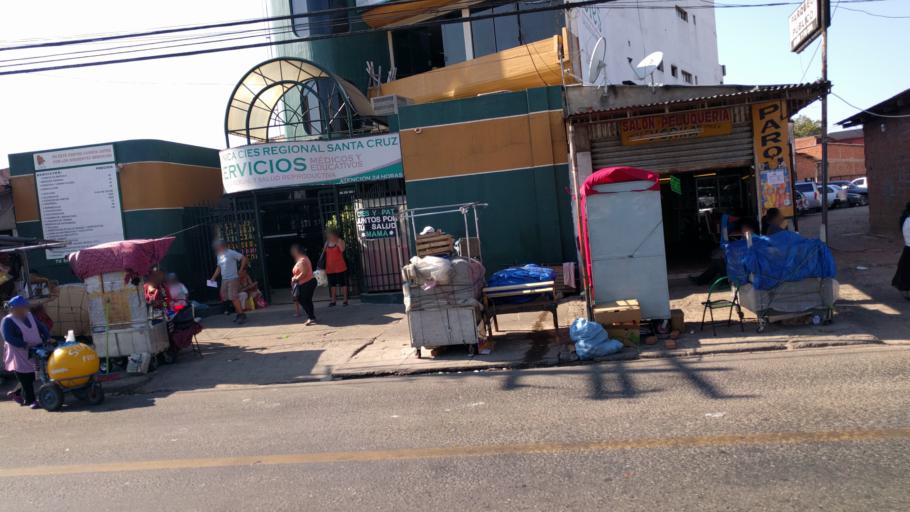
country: BO
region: Santa Cruz
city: Santa Cruz de la Sierra
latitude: -17.7959
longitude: -63.1902
